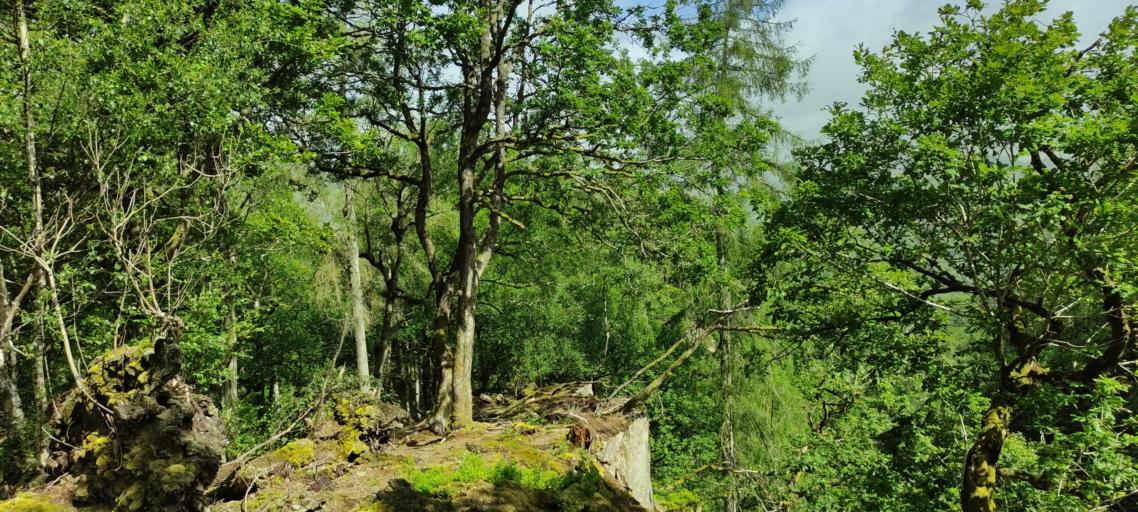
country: GB
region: England
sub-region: Cumbria
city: Millom
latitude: 54.3846
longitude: -3.2734
